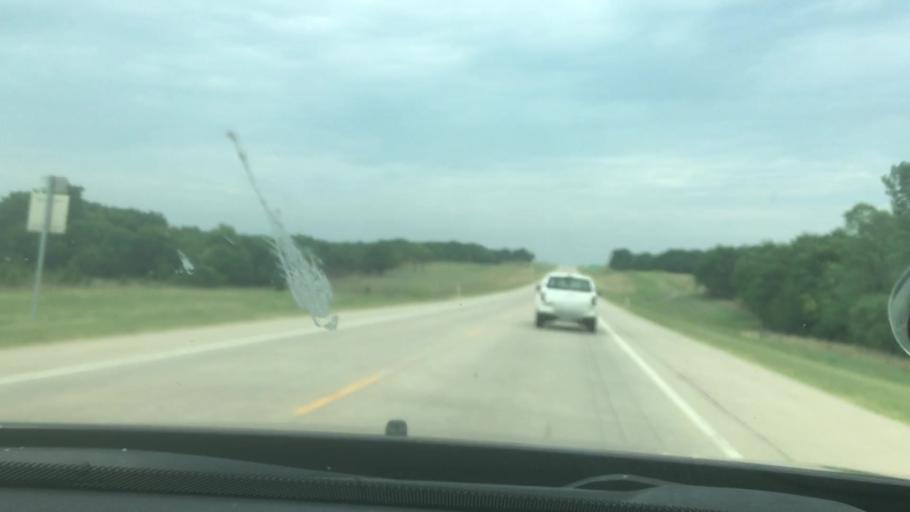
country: US
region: Oklahoma
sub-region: Murray County
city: Sulphur
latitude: 34.6119
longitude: -96.8759
